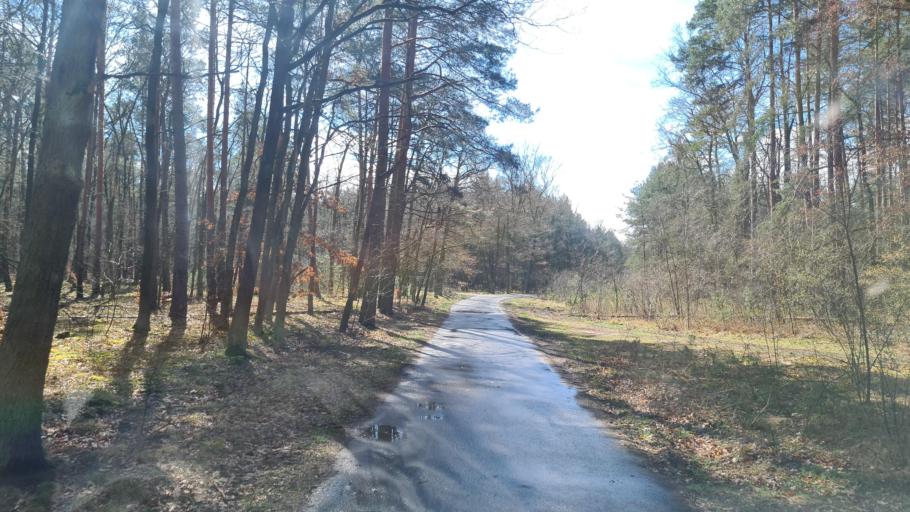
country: DE
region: Brandenburg
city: Altdobern
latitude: 51.7035
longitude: 14.0379
